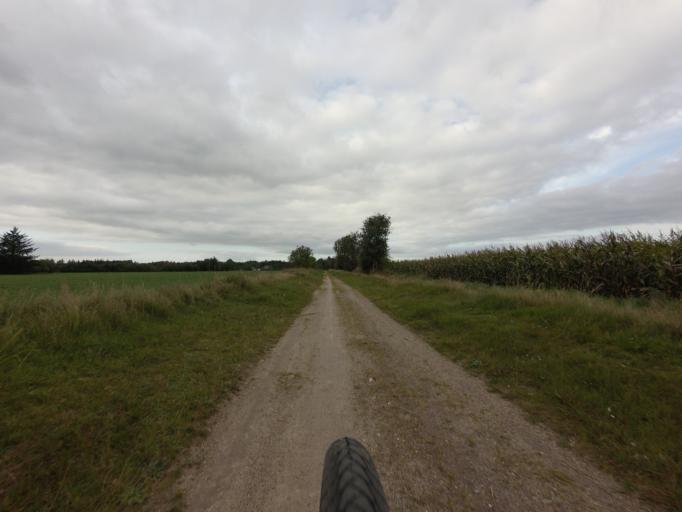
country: DK
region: South Denmark
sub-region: Billund Kommune
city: Billund
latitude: 55.8346
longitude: 9.0299
